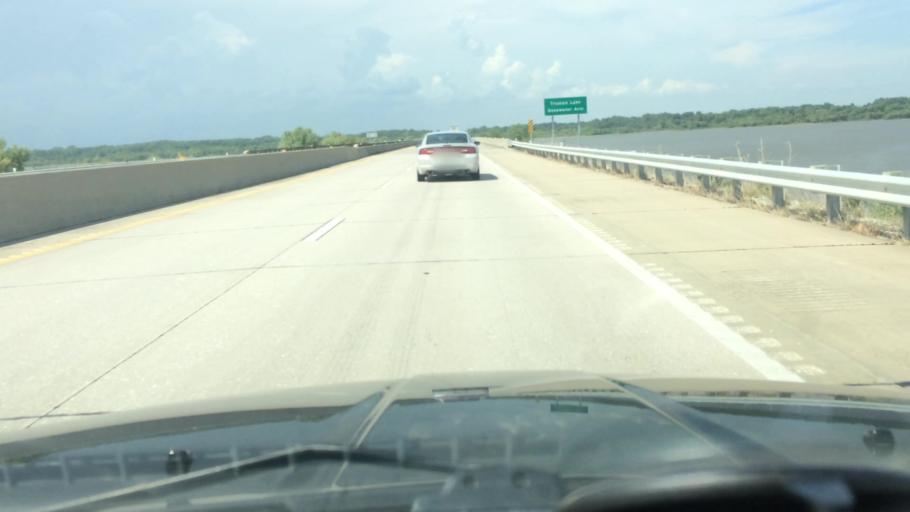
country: US
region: Missouri
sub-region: Henry County
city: Clinton
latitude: 38.2750
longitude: -93.7598
